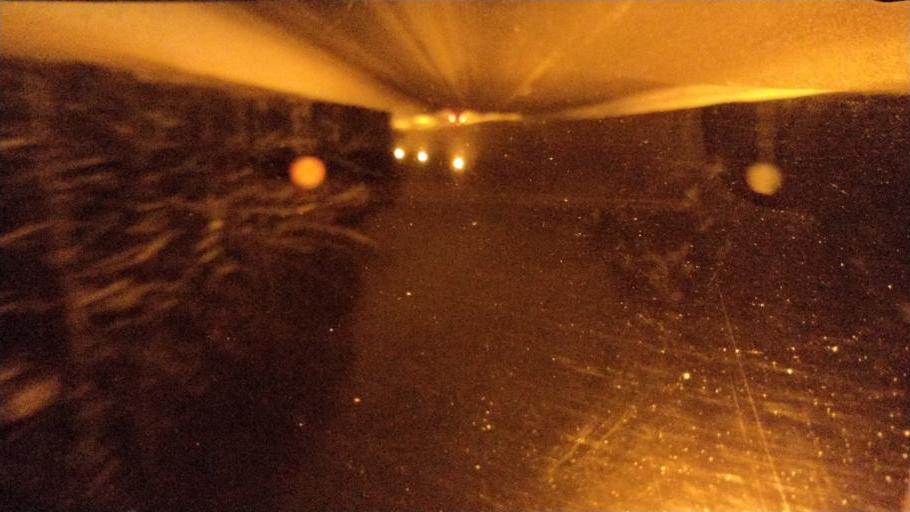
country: FI
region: Lapland
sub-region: Rovaniemi
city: Rovaniemi
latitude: 66.2627
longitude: 25.3398
